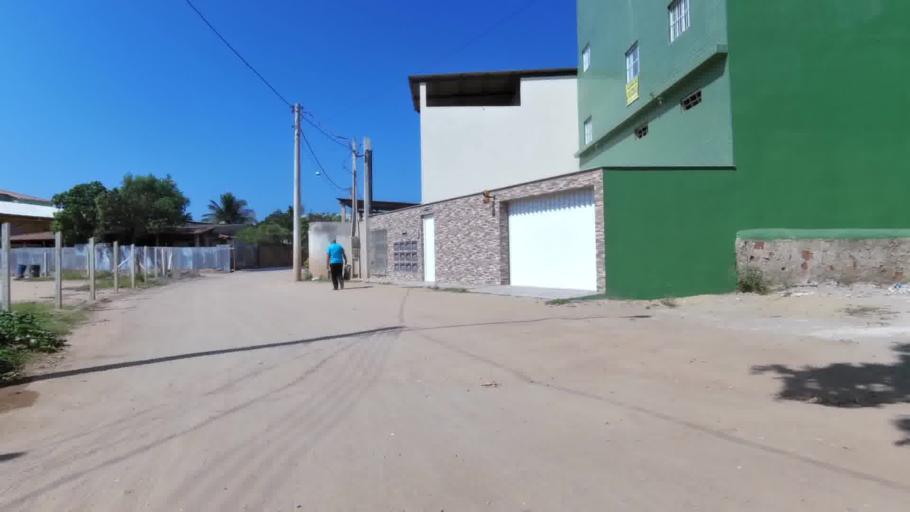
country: BR
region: Espirito Santo
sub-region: Itapemirim
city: Itapemirim
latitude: -21.0233
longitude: -40.8172
